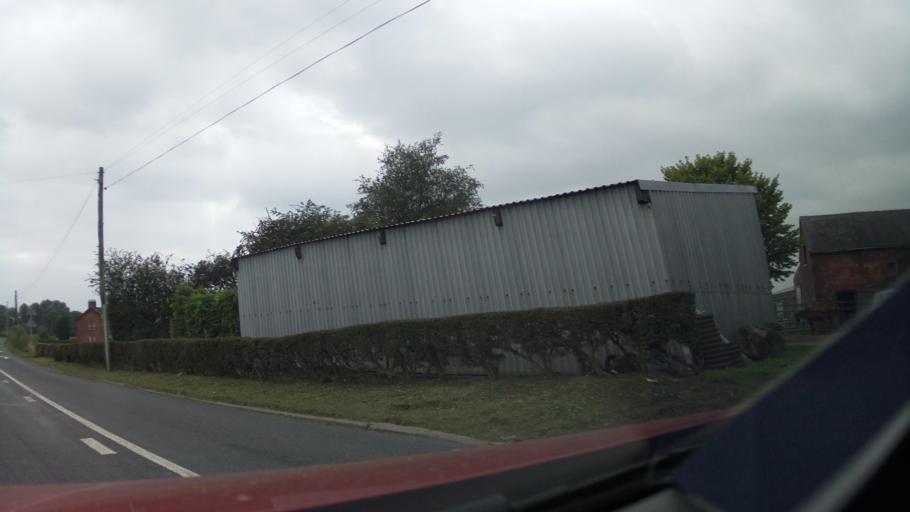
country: GB
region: England
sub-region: Staffordshire
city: Cheadle
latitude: 53.0178
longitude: -2.0104
